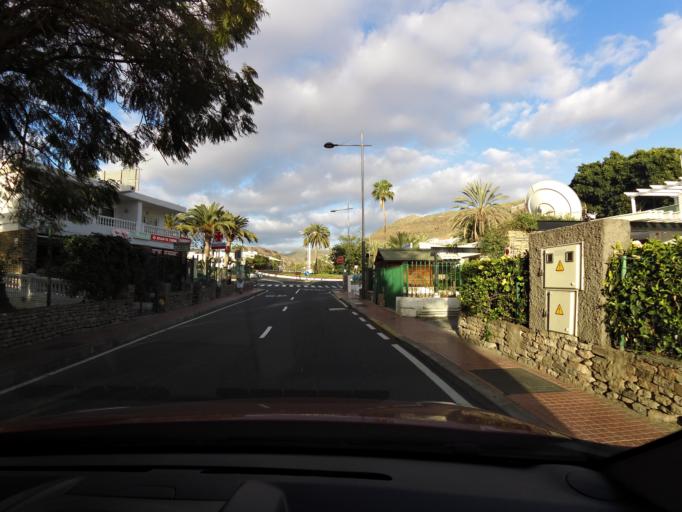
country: ES
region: Canary Islands
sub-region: Provincia de Las Palmas
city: Puerto Rico
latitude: 27.7874
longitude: -15.7116
